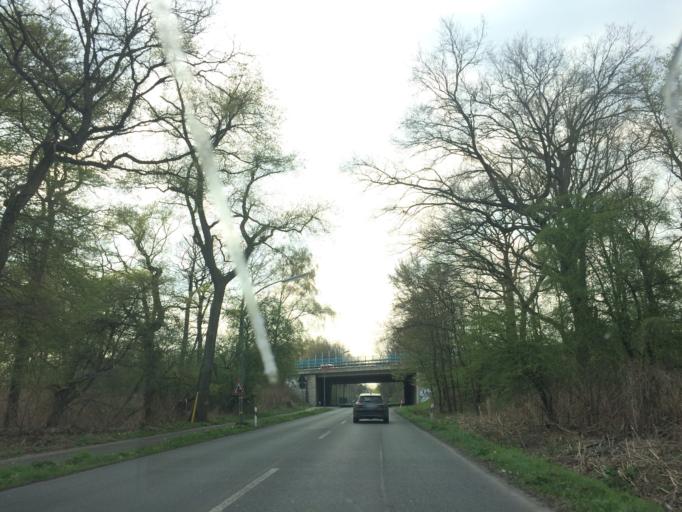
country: DE
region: North Rhine-Westphalia
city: Herten
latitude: 51.5704
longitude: 7.1241
